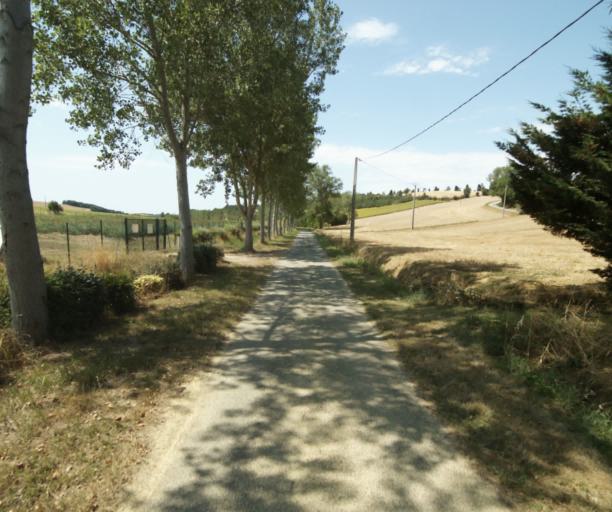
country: FR
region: Midi-Pyrenees
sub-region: Departement de la Haute-Garonne
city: Saint-Felix-Lauragais
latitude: 43.4562
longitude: 1.8799
